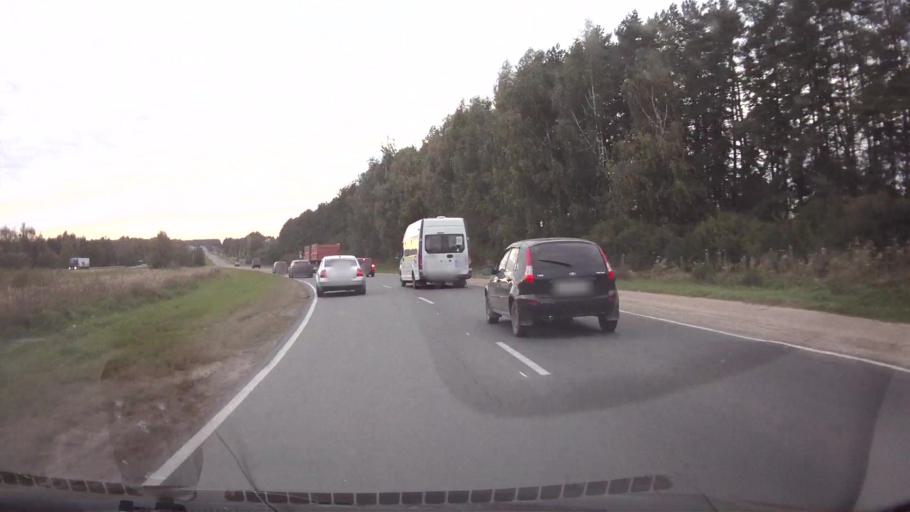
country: RU
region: Mariy-El
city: Sovetskiy
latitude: 56.7474
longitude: 48.2299
